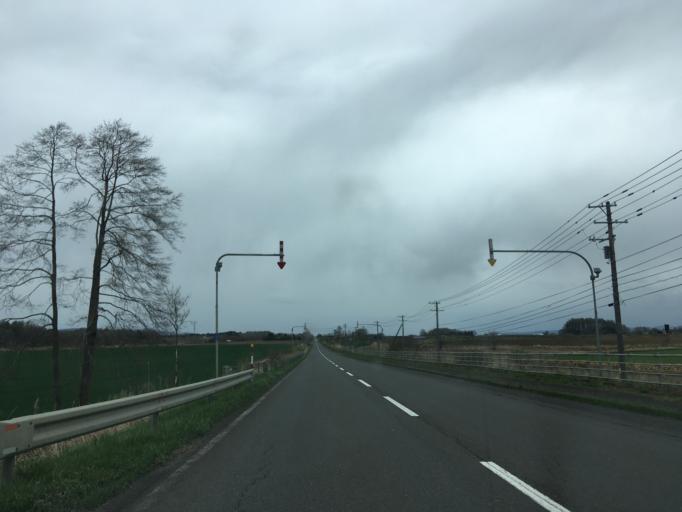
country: JP
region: Hokkaido
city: Chitose
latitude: 42.9040
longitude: 141.8128
